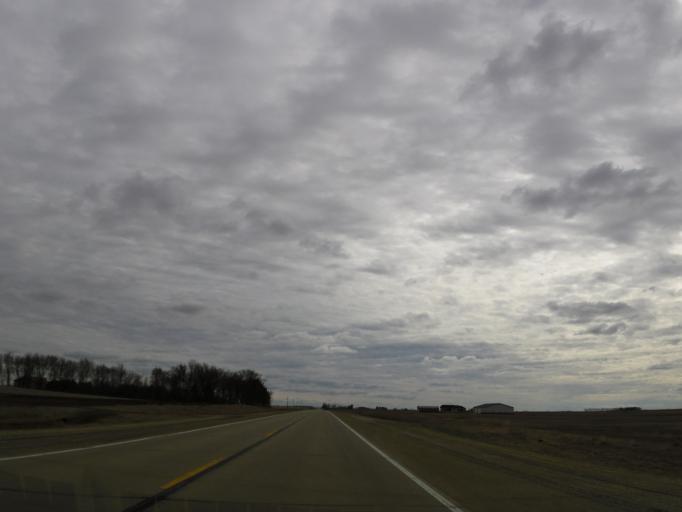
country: US
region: Iowa
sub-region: Howard County
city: Cresco
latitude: 43.4237
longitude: -92.2987
